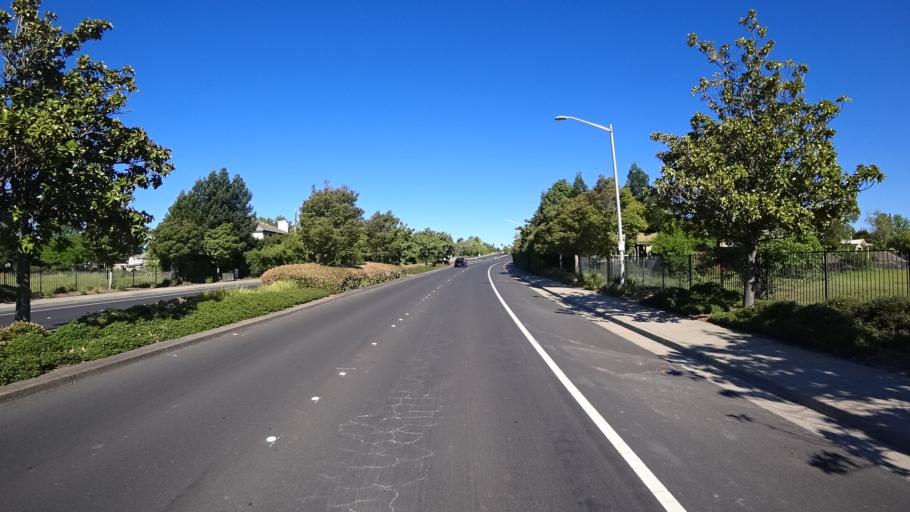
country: US
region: California
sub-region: Placer County
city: Rocklin
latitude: 38.8153
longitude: -121.2678
